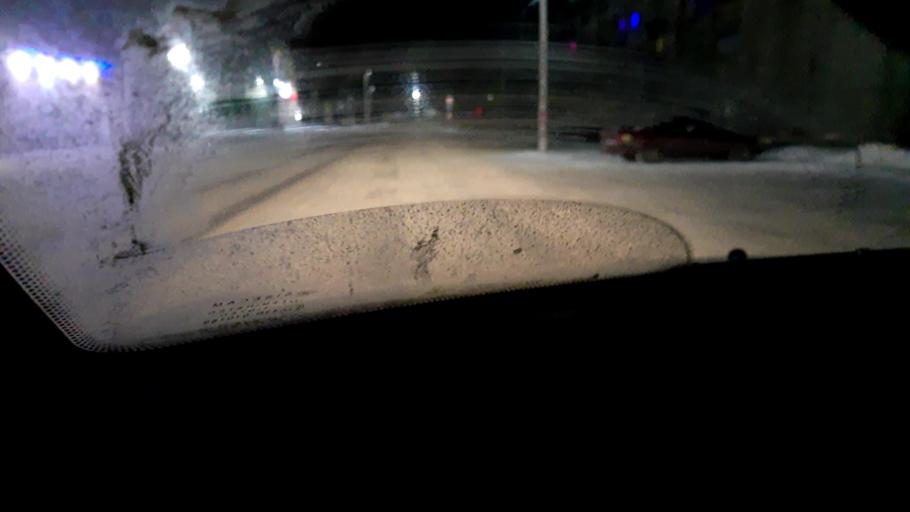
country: RU
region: Nizjnij Novgorod
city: Bogorodsk
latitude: 56.0998
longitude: 43.4738
